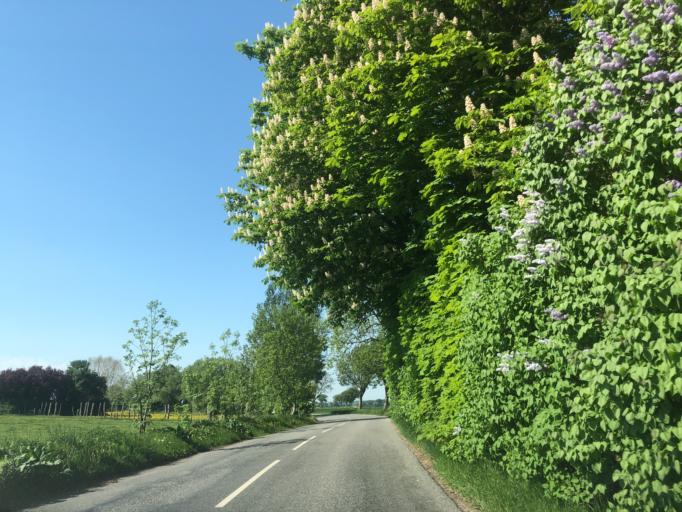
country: DK
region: Zealand
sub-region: Roskilde Kommune
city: Viby
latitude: 55.5757
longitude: 12.0298
